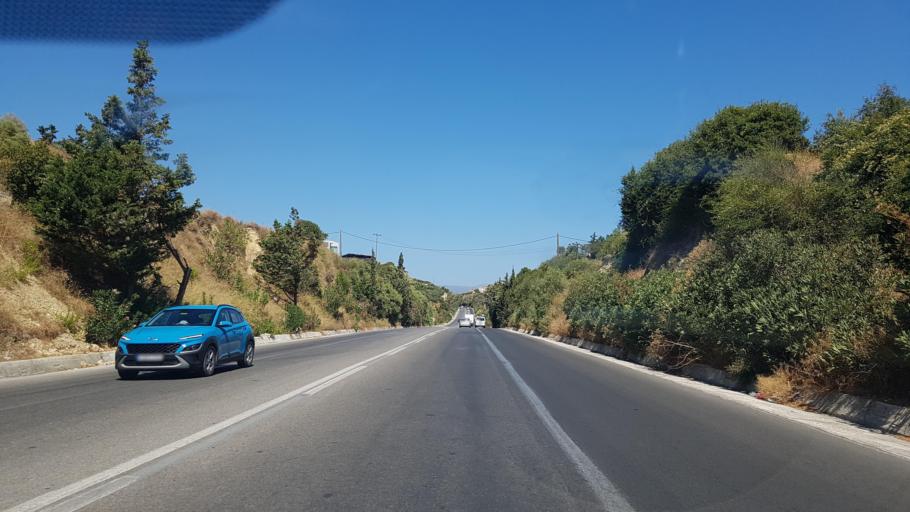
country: GR
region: Crete
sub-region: Nomos Chanias
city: Agia Marina
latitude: 35.5095
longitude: 23.9329
